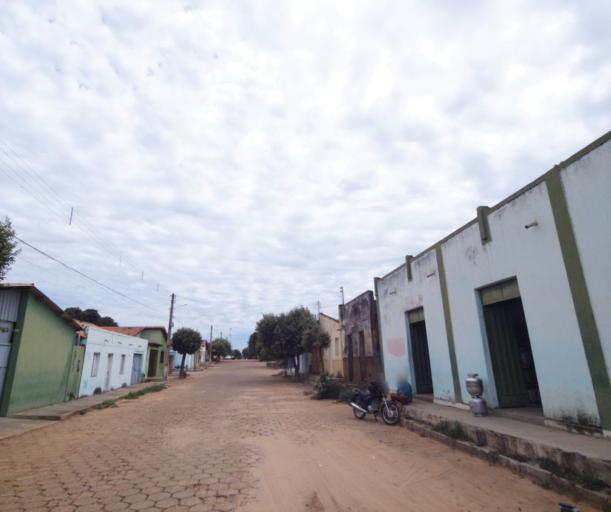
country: BR
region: Bahia
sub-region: Carinhanha
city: Carinhanha
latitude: -14.2133
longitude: -44.2834
